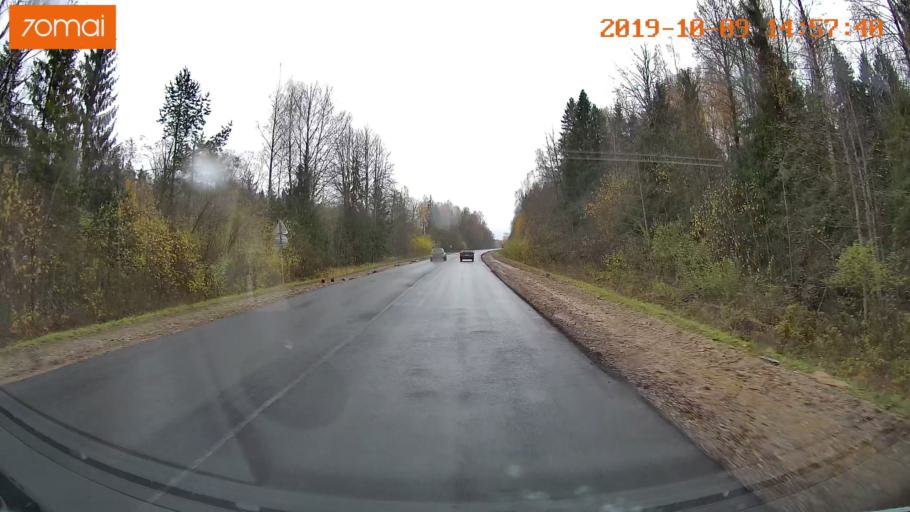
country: RU
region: Kostroma
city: Chistyye Bory
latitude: 58.3352
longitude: 41.6519
